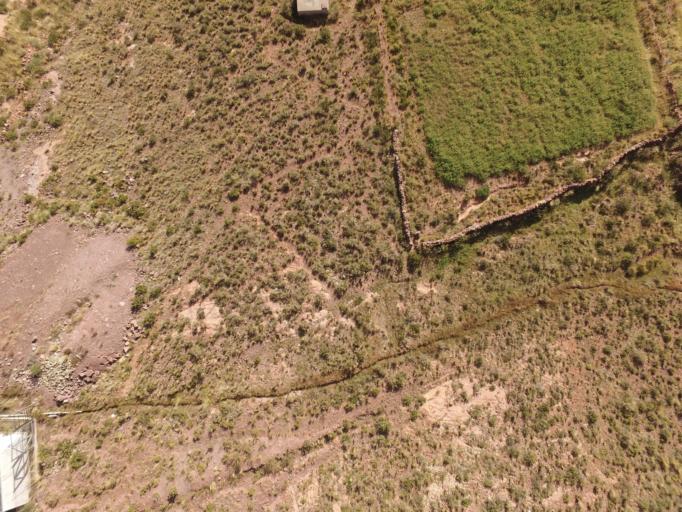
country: BO
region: Oruro
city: Challapata
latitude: -18.6906
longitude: -66.7557
